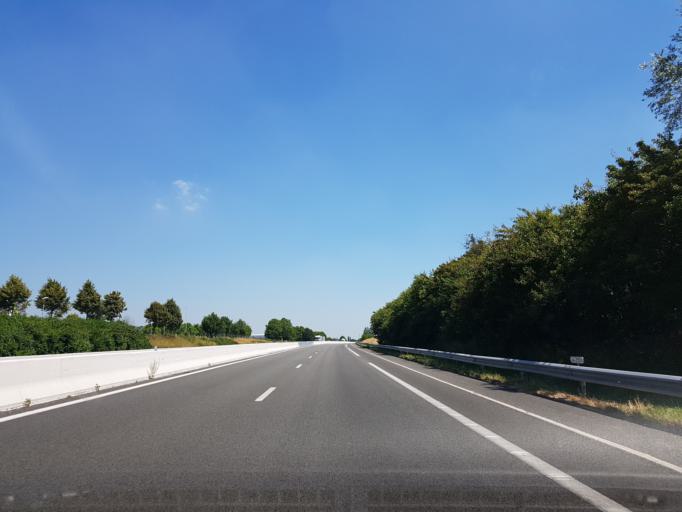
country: FR
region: Nord-Pas-de-Calais
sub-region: Departement du Nord
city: Neuville-Saint-Remy
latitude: 50.1901
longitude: 3.1973
